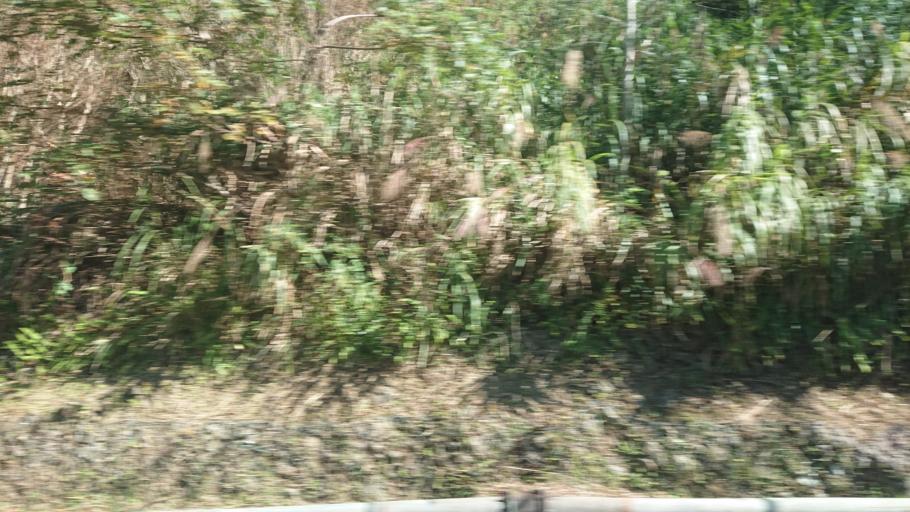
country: TW
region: Taiwan
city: Lugu
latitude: 23.4974
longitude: 120.7824
